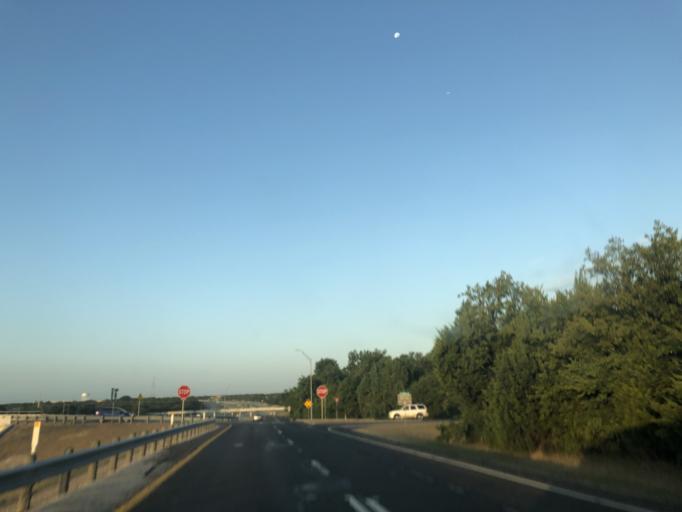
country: US
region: Texas
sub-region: Dallas County
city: Cedar Hill
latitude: 32.5795
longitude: -96.9572
